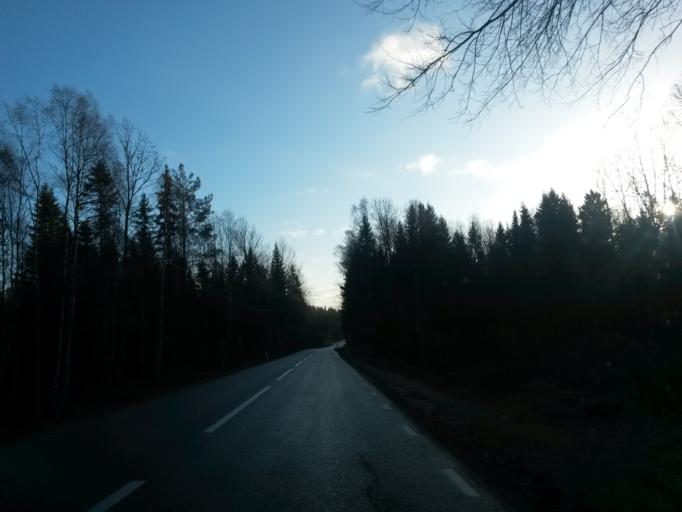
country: SE
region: Vaestra Goetaland
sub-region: Boras Kommun
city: Boras
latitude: 57.8931
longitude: 12.9249
